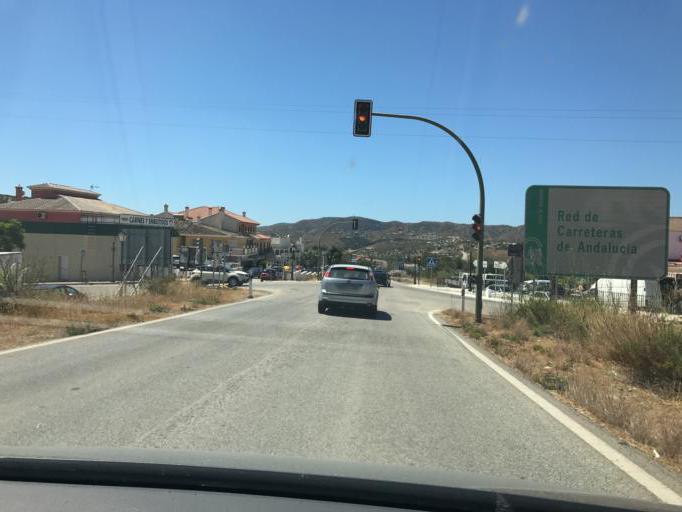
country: ES
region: Andalusia
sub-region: Provincia de Malaga
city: Vinuela
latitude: 36.8899
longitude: -4.1465
